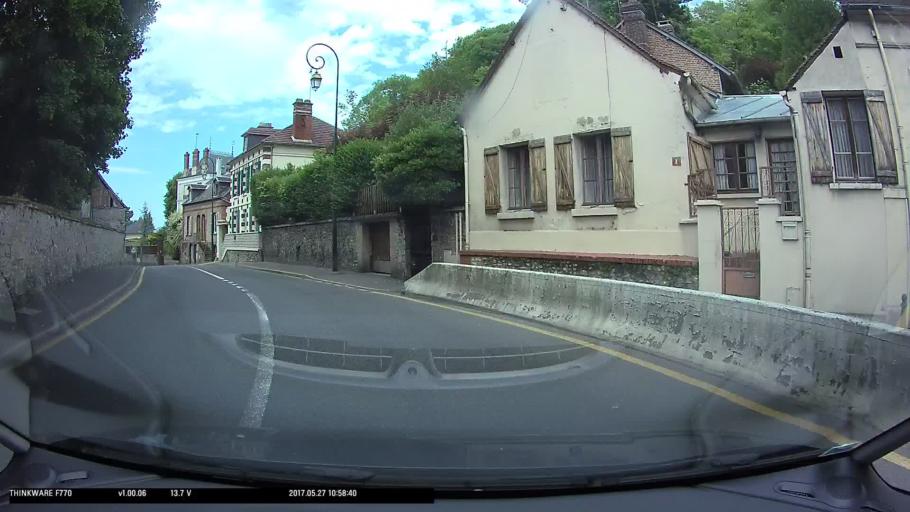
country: FR
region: Picardie
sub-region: Departement de l'Oise
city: Chaumont-en-Vexin
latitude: 49.2623
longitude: 1.8790
